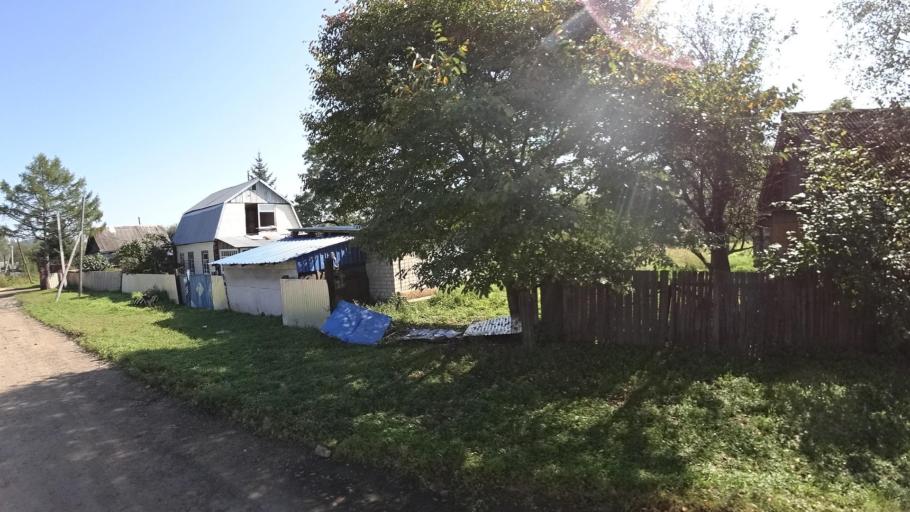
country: RU
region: Jewish Autonomous Oblast
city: Bira
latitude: 48.9920
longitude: 132.4638
